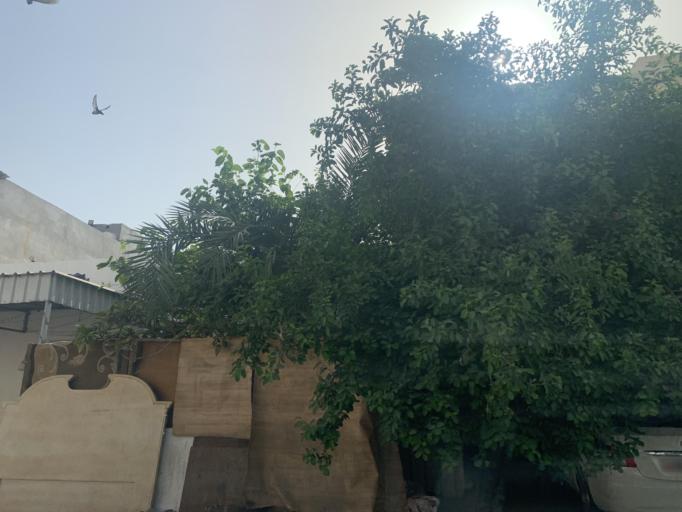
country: BH
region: Northern
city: Sitrah
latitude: 26.1665
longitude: 50.6068
